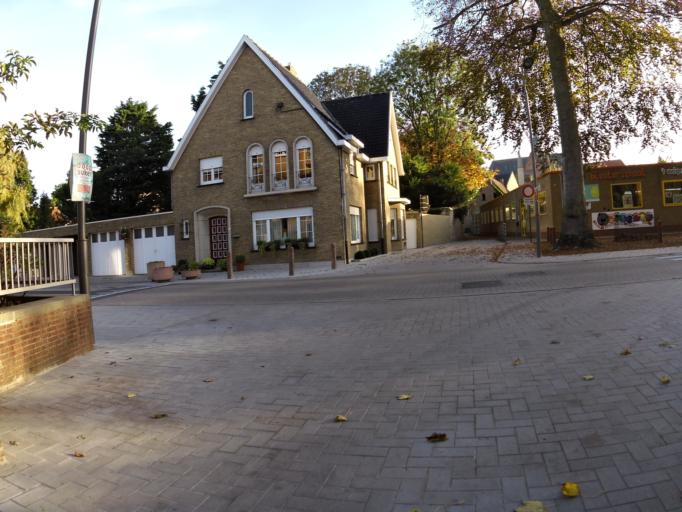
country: BE
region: Flanders
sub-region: Provincie West-Vlaanderen
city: Veurne
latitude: 51.0754
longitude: 2.6611
